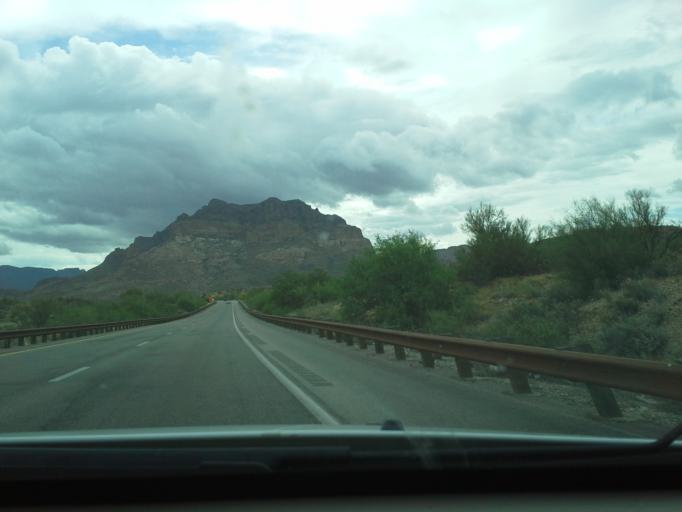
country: US
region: Arizona
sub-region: Pinal County
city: Superior
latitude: 33.2741
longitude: -111.1985
